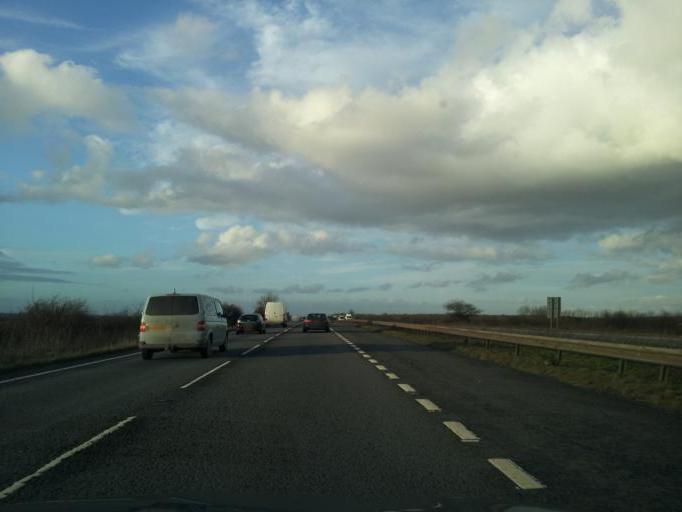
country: GB
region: England
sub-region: District of Rutland
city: Clipsham
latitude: 52.7850
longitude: -0.6110
